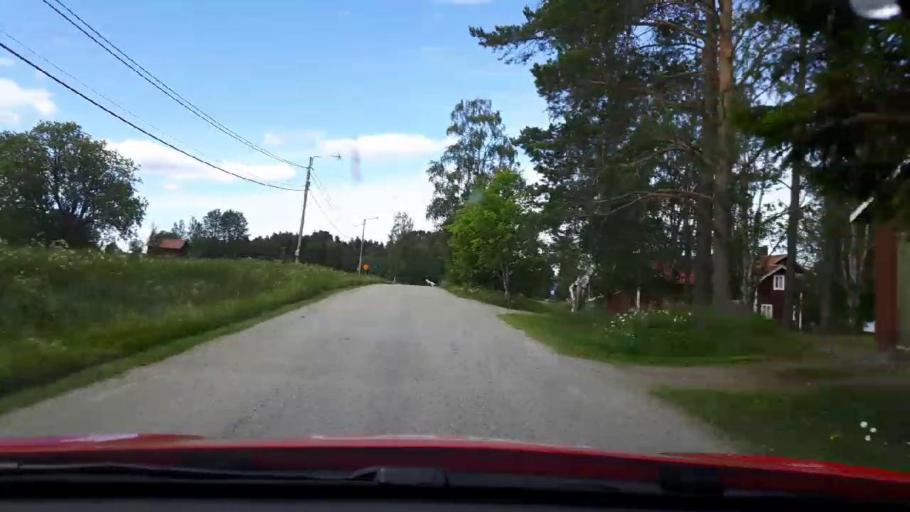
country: SE
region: Jaemtland
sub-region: Bergs Kommun
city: Hoverberg
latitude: 62.8171
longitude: 14.4589
